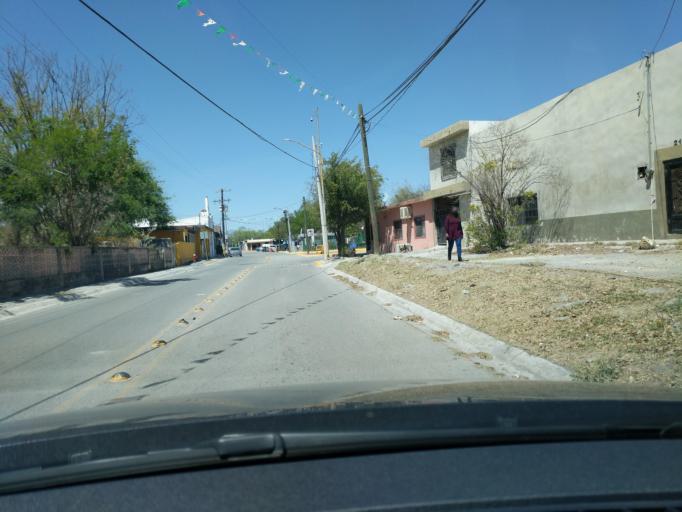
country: MX
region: Nuevo Leon
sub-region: Apodaca
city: Artemio Trevino
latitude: 25.8130
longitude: -100.1505
